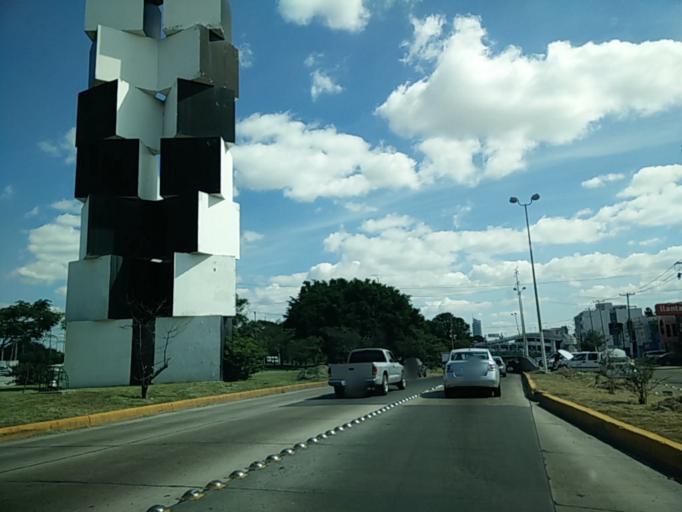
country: MX
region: Jalisco
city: Guadalajara
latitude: 20.6775
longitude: -103.4170
